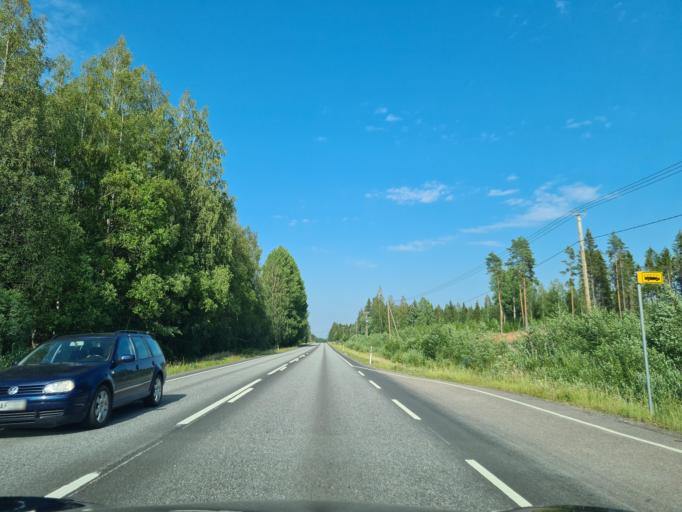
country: FI
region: Satakunta
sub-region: Pori
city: Laengelmaeki
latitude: 61.7766
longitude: 22.1909
